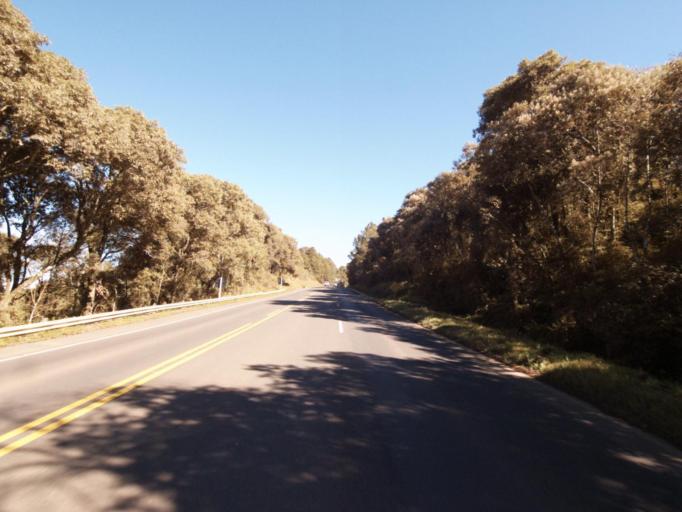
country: BR
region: Santa Catarina
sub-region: Joacaba
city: Joacaba
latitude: -26.9824
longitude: -51.7879
